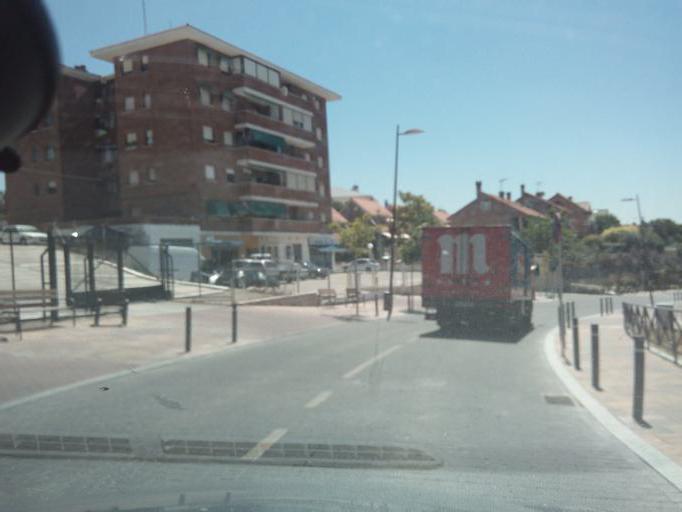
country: ES
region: Madrid
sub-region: Provincia de Madrid
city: Cobena
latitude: 40.5717
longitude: -3.5041
